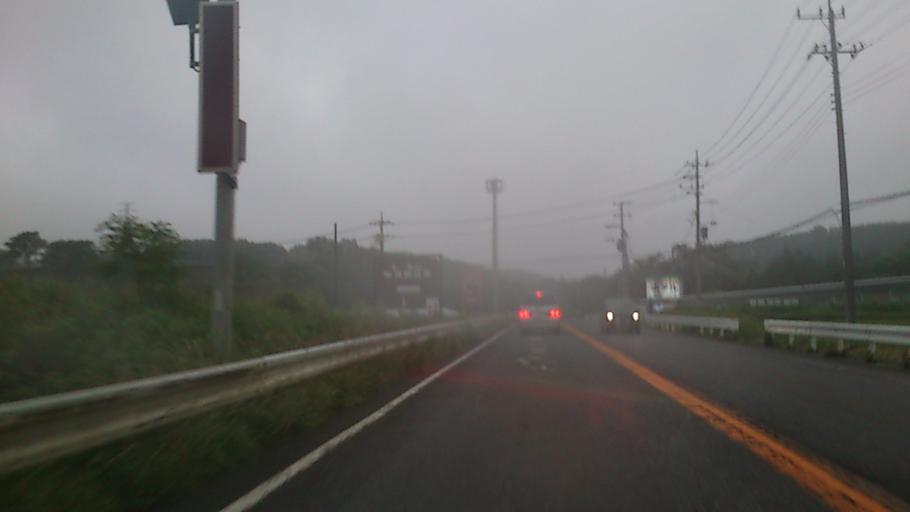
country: JP
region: Tochigi
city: Kuroiso
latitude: 37.0809
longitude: 140.1299
